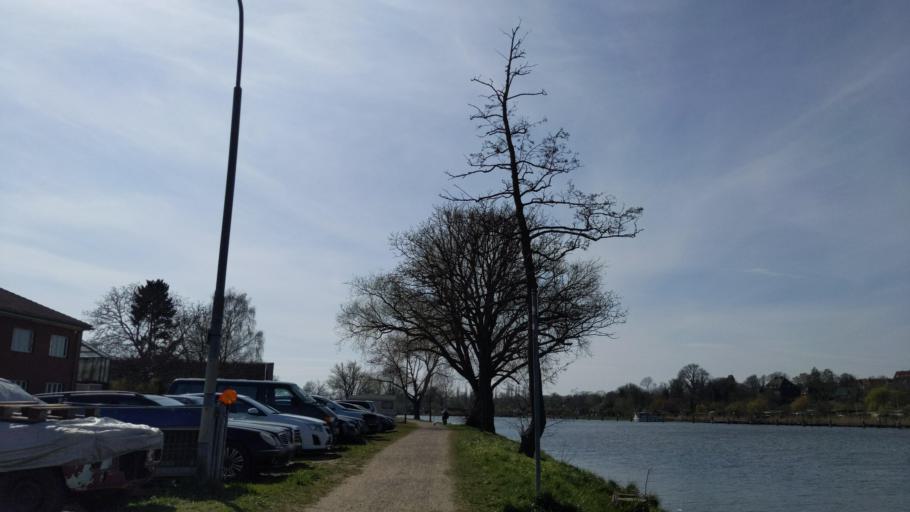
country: DE
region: Schleswig-Holstein
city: Luebeck
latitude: 53.8547
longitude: 10.6793
